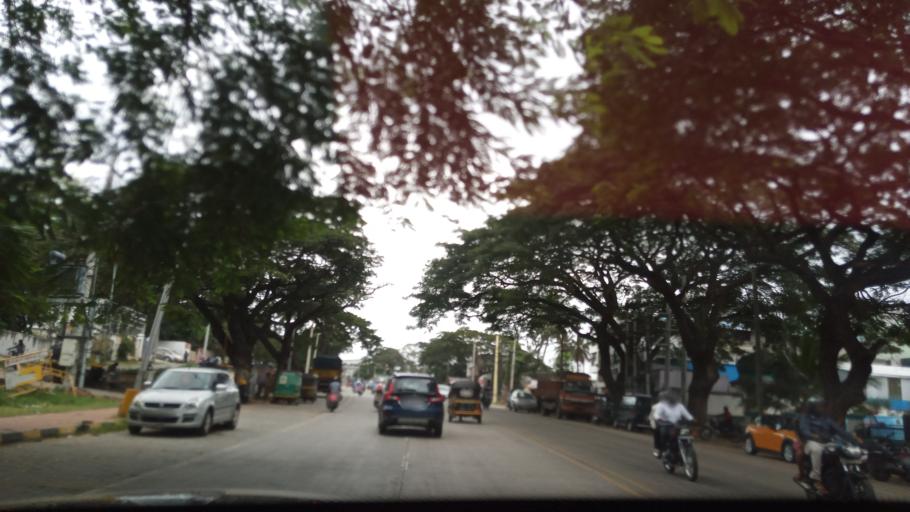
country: IN
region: Karnataka
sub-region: Mysore
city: Mysore
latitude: 12.3283
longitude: 76.6447
